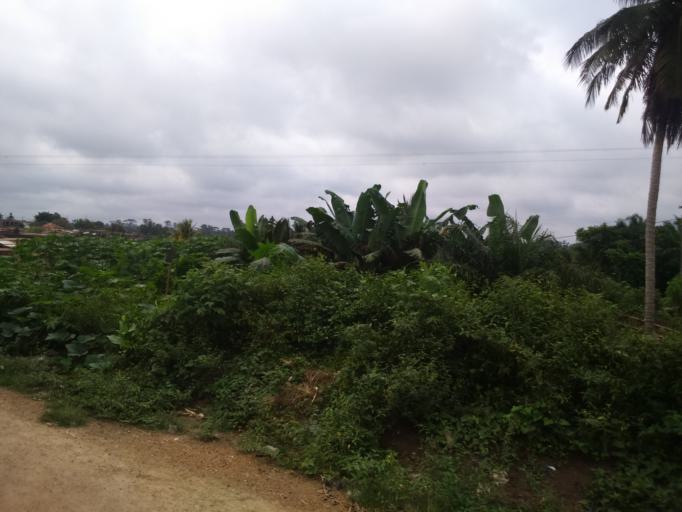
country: CI
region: Lagunes
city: Agou
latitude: 6.0562
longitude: -4.0974
